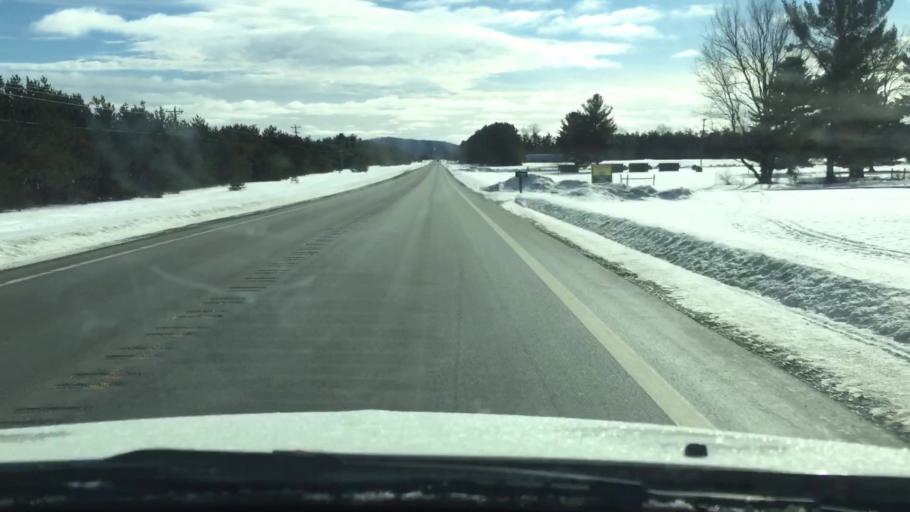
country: US
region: Michigan
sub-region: Antrim County
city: Mancelona
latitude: 44.9286
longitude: -85.0509
